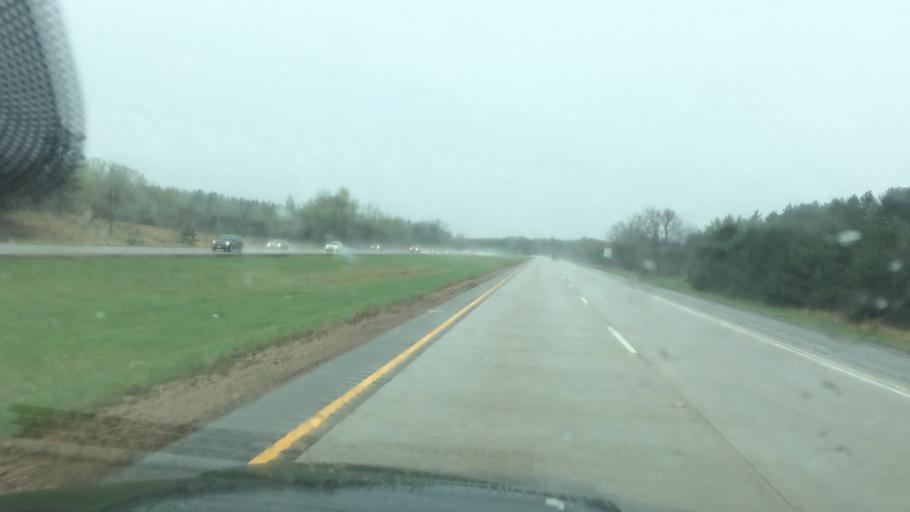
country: US
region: Wisconsin
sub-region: Marathon County
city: Mosinee
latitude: 44.6678
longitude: -89.6428
